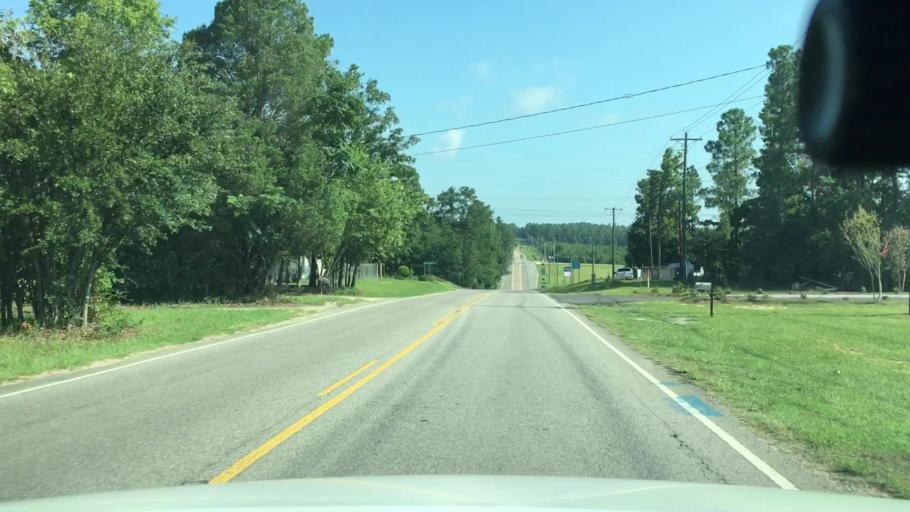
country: US
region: South Carolina
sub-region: Aiken County
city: Graniteville
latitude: 33.5798
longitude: -81.8359
